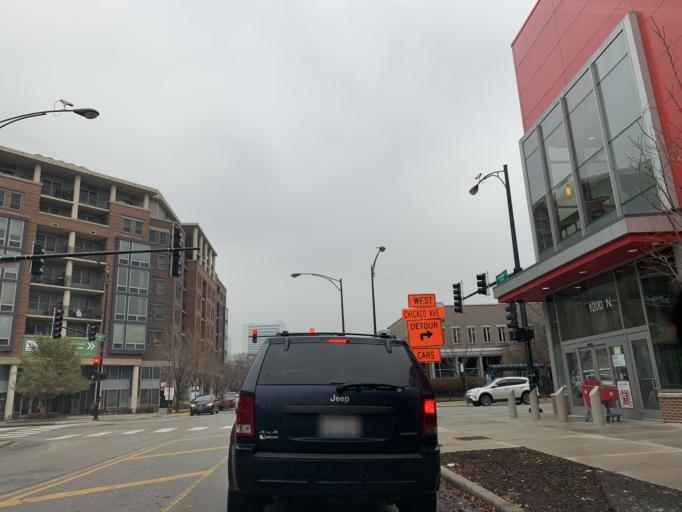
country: US
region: Illinois
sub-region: Cook County
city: Chicago
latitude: 41.9040
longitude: -87.6432
